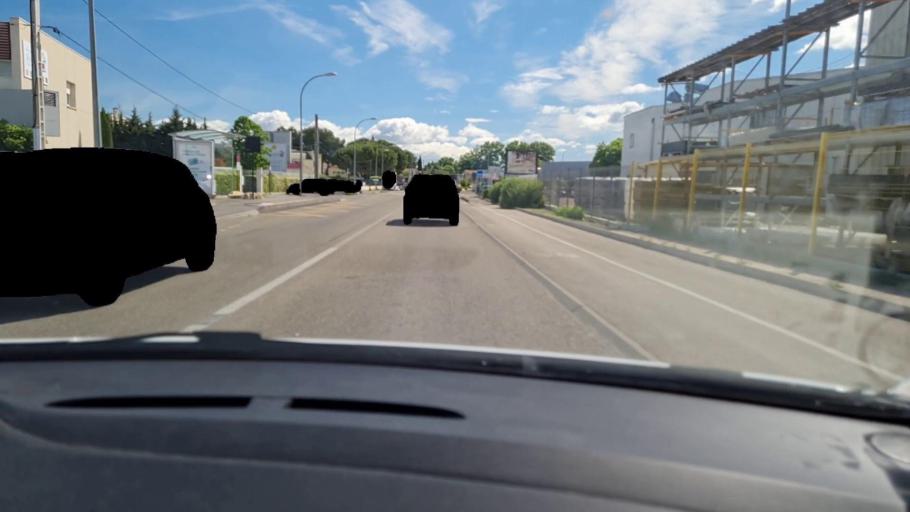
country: FR
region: Languedoc-Roussillon
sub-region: Departement du Gard
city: Milhaud
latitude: 43.8130
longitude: 4.3216
